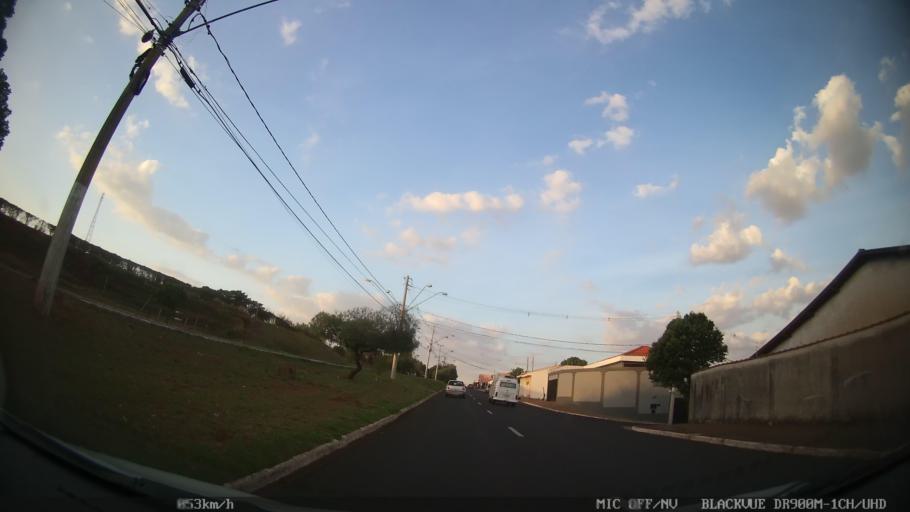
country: BR
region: Sao Paulo
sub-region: Ribeirao Preto
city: Ribeirao Preto
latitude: -21.1382
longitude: -47.8504
